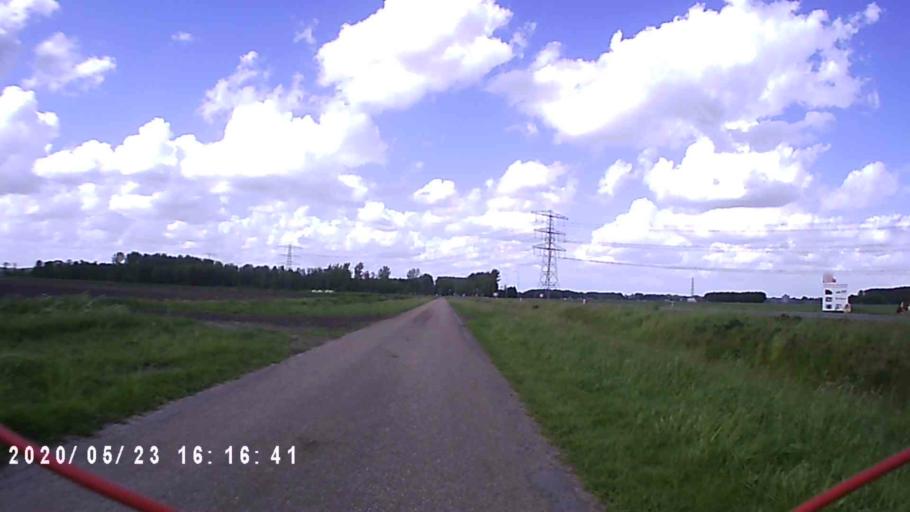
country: NL
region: Groningen
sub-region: Gemeente Appingedam
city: Appingedam
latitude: 53.2631
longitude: 6.8750
